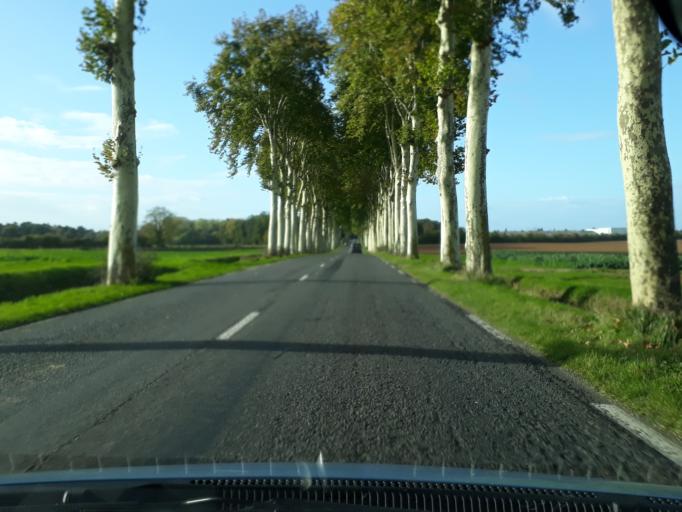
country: FR
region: Ile-de-France
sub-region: Departement de Seine-et-Marne
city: La Chapelle-la-Reine
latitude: 48.3287
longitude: 2.5863
